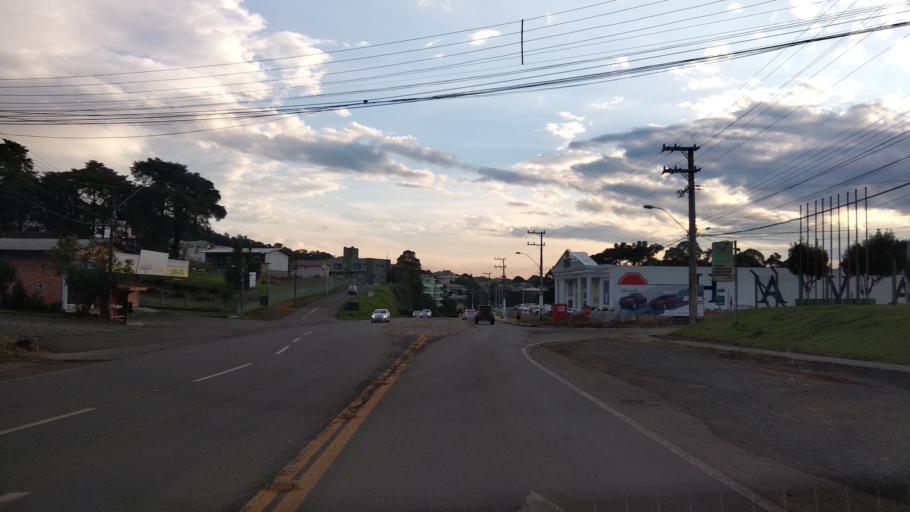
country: BR
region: Santa Catarina
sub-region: Videira
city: Videira
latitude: -26.9999
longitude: -51.1206
